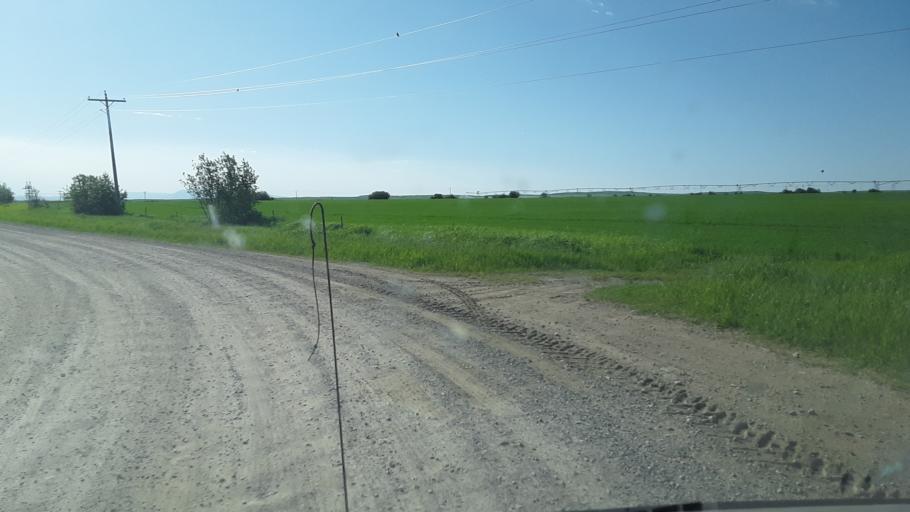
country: US
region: Montana
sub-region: Carbon County
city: Red Lodge
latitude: 45.3491
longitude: -109.1602
